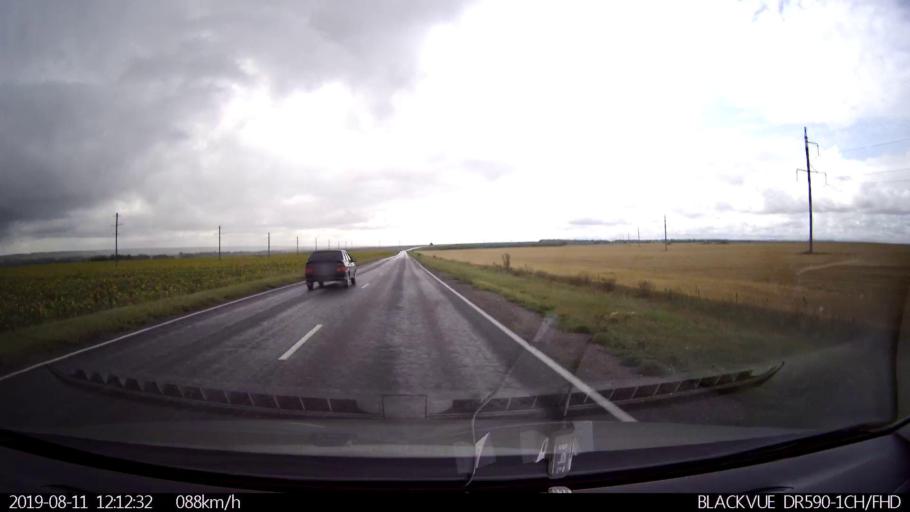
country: RU
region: Ulyanovsk
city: Silikatnyy
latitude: 53.9719
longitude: 47.9962
